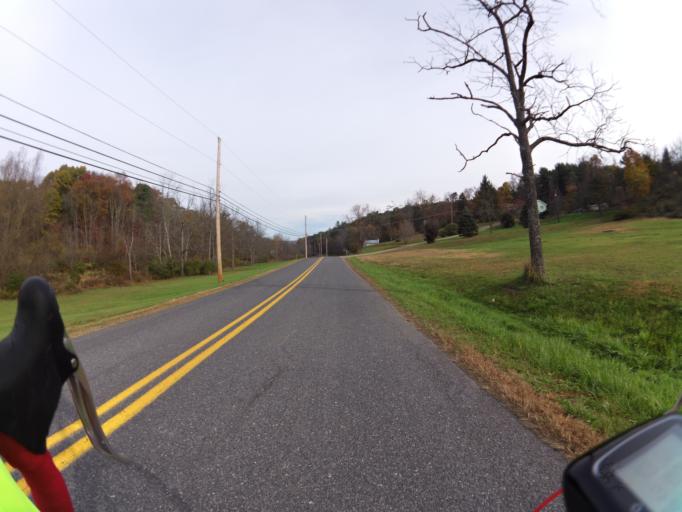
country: US
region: Pennsylvania
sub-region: Union County
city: New Columbia
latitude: 41.0316
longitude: -76.9213
